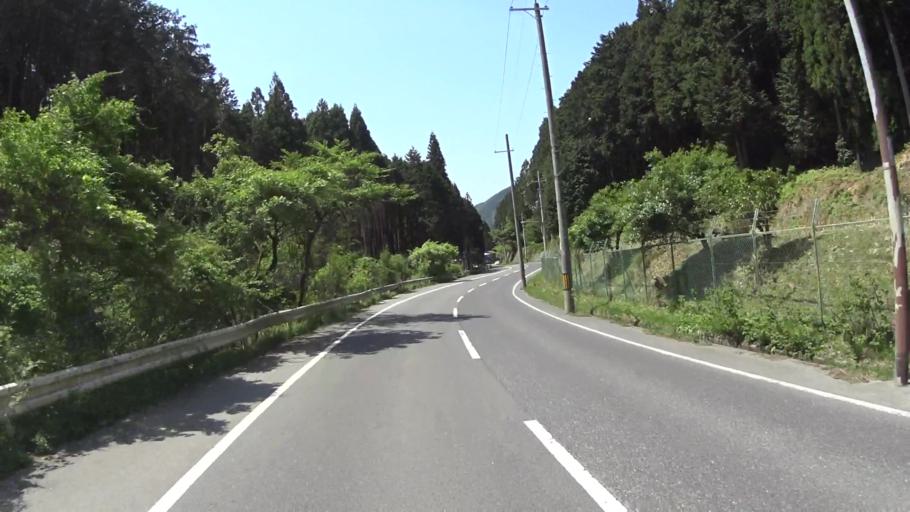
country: JP
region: Shiga Prefecture
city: Kitahama
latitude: 35.1550
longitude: 135.8486
